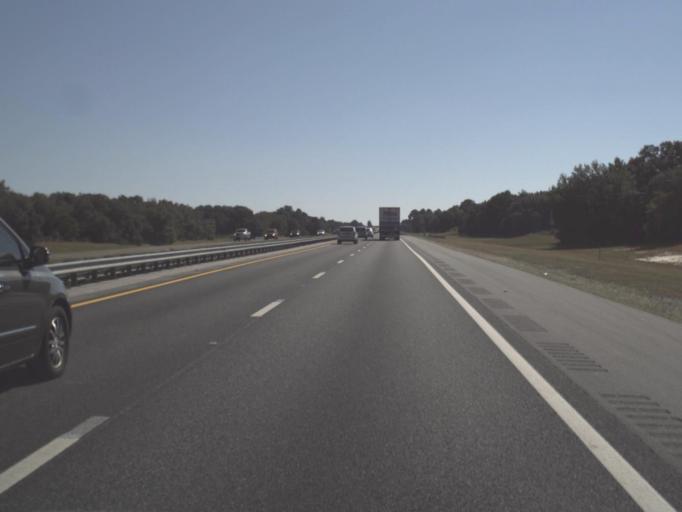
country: US
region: Florida
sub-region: Lake County
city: Hawthorne
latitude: 28.7261
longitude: -81.9080
